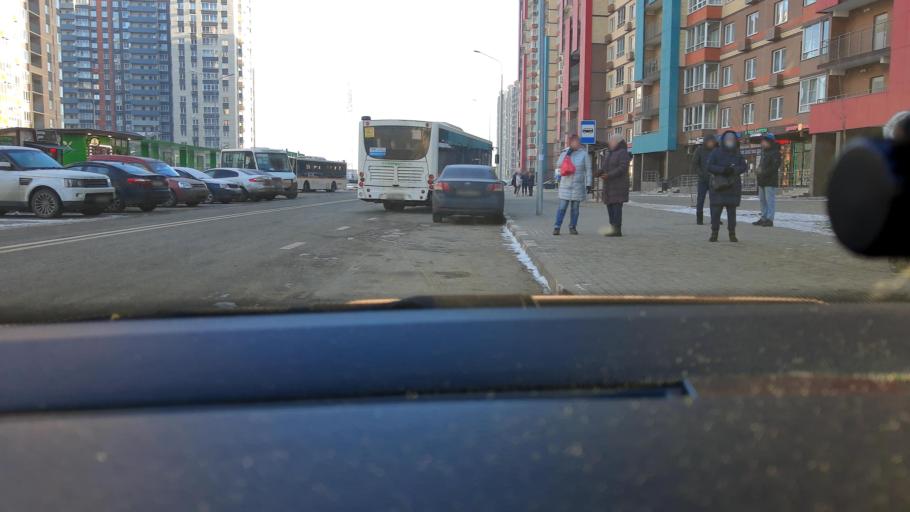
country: RU
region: Moskovskaya
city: Petrovskaya
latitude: 55.5591
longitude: 37.8153
